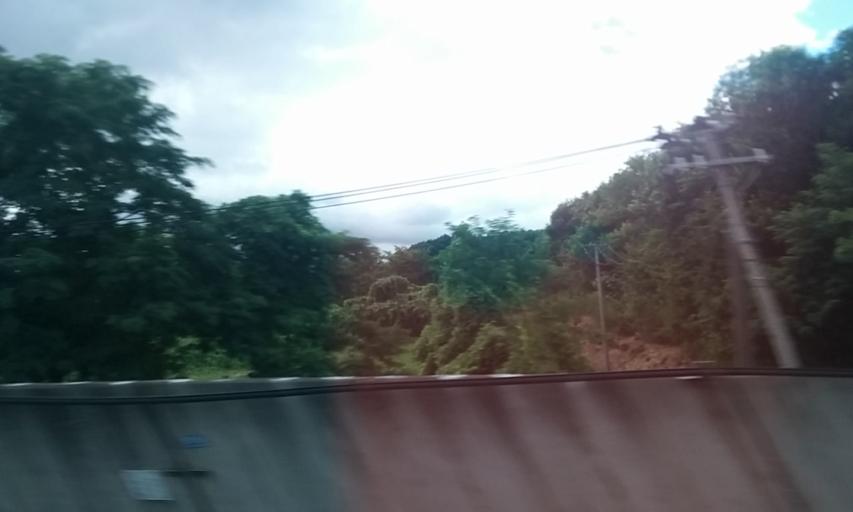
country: JP
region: Fukushima
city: Sukagawa
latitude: 37.2210
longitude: 140.2801
